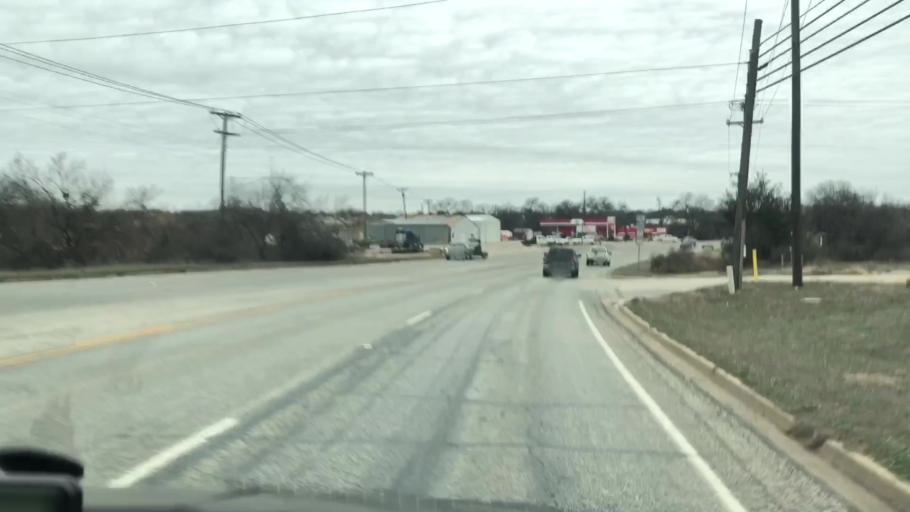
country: US
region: Texas
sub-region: Jack County
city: Jacksboro
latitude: 33.2110
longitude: -98.1580
